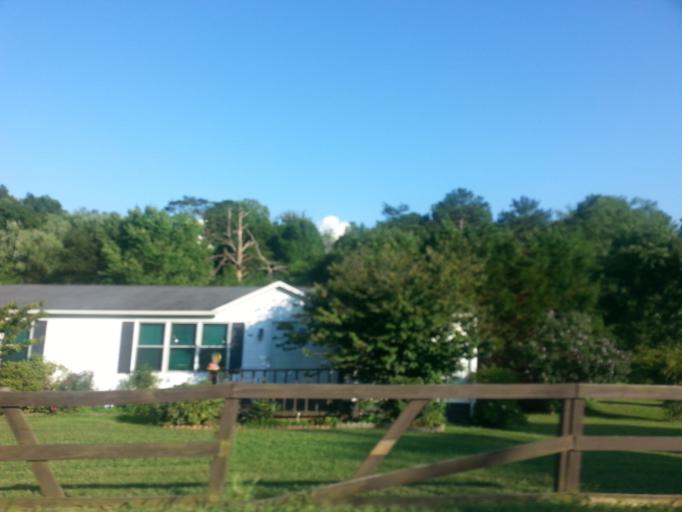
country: US
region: Tennessee
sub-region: Blount County
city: Wildwood
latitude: 35.7362
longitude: -83.8898
